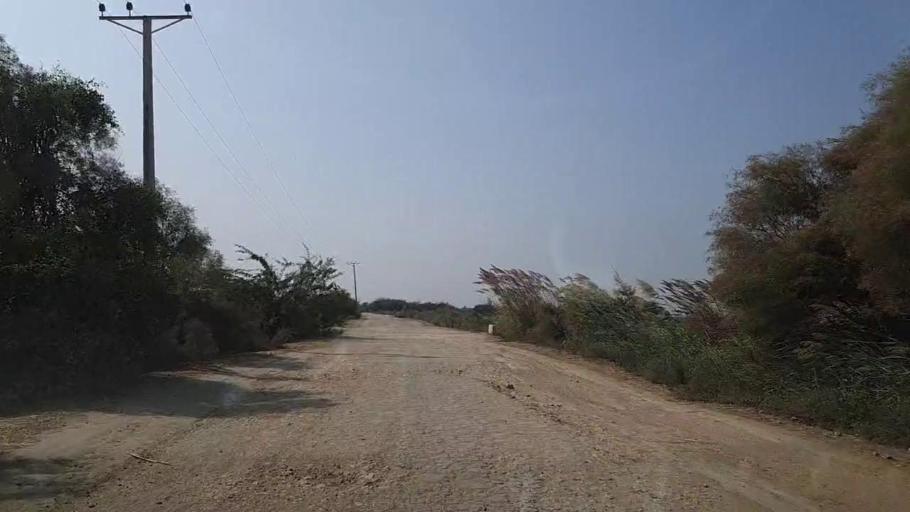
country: PK
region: Sindh
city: Mirpur Sakro
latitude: 24.5455
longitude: 67.6104
